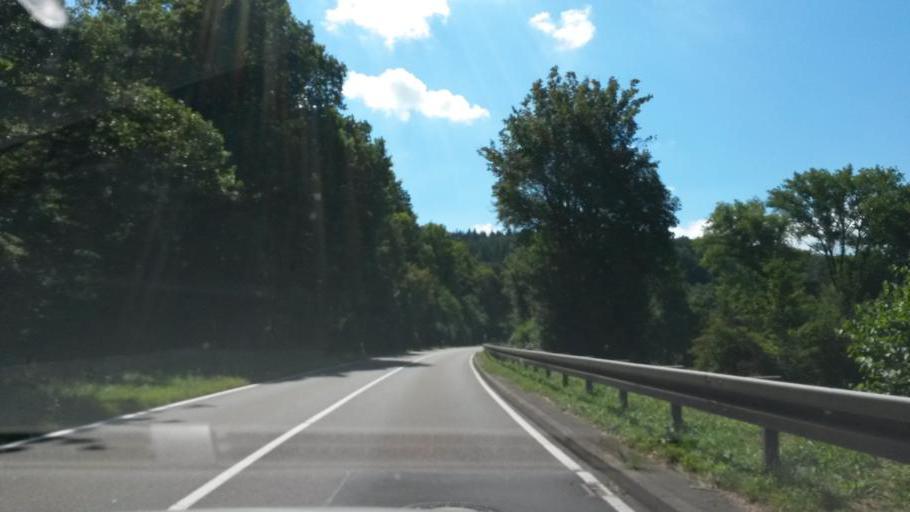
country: DE
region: Baden-Wuerttemberg
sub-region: Karlsruhe Region
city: Ispringen
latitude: 48.9246
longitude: 8.6367
